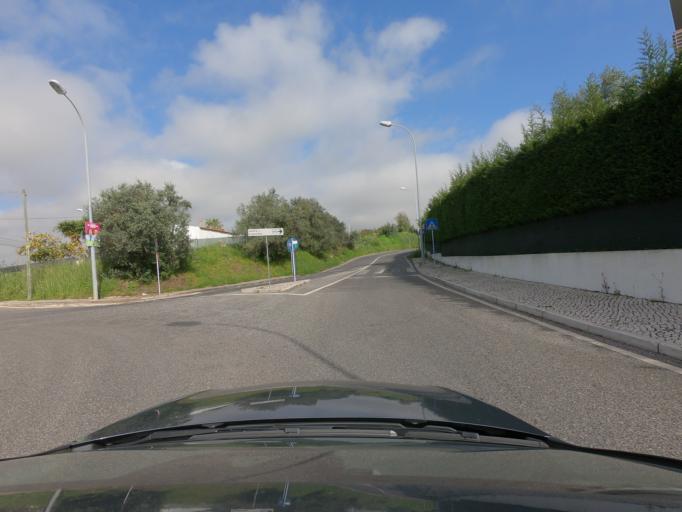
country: PT
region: Lisbon
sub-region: Oeiras
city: Quejas
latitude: 38.7189
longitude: -9.2677
